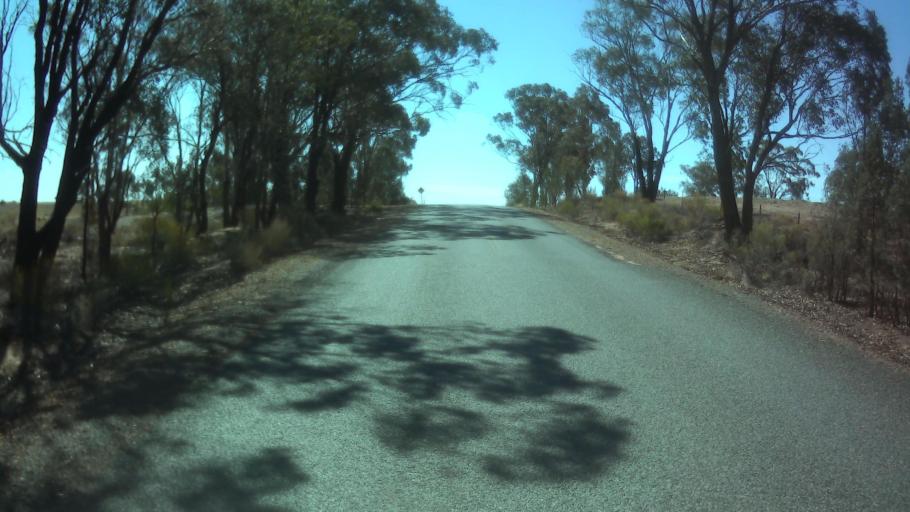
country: AU
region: New South Wales
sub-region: Weddin
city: Grenfell
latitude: -33.7576
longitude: 147.8565
